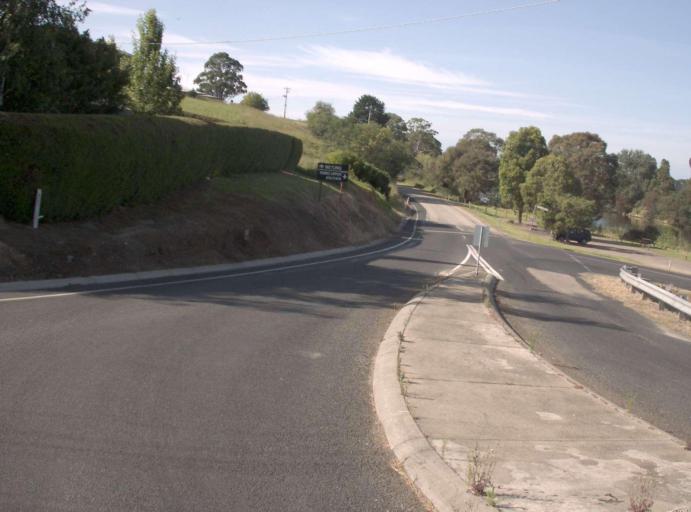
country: AU
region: Victoria
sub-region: East Gippsland
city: Lakes Entrance
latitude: -37.8221
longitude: 147.8637
